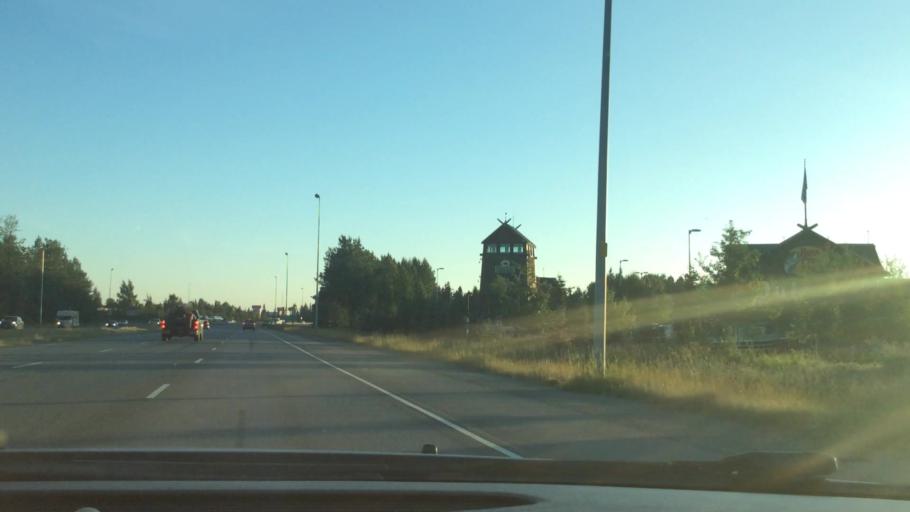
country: US
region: Alaska
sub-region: Anchorage Municipality
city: Anchorage
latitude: 61.2190
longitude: -149.8175
